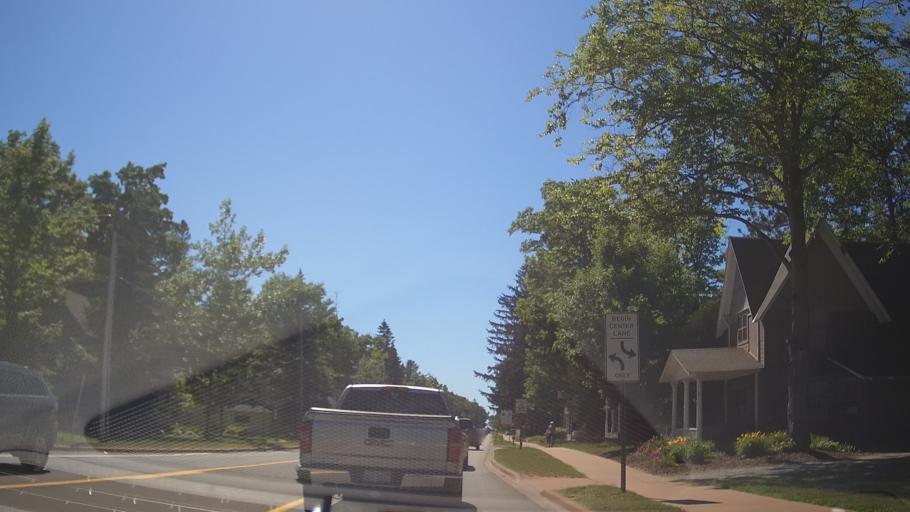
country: US
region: Michigan
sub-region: Emmet County
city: Petoskey
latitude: 45.3861
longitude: -84.9253
